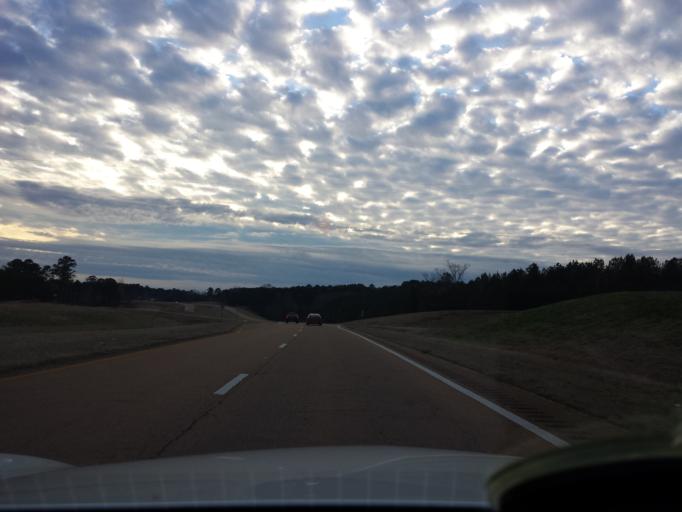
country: US
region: Mississippi
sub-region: Winston County
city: Louisville
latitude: 33.2408
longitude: -88.9755
